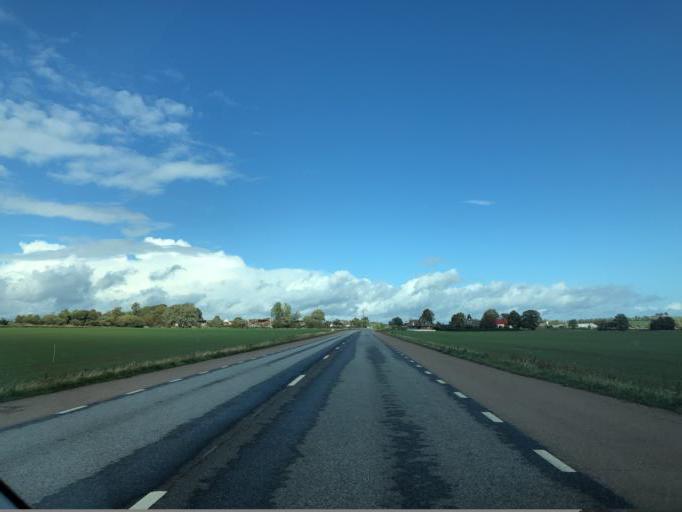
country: SE
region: Skane
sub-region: Helsingborg
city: Glumslov
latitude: 55.9136
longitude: 12.8285
